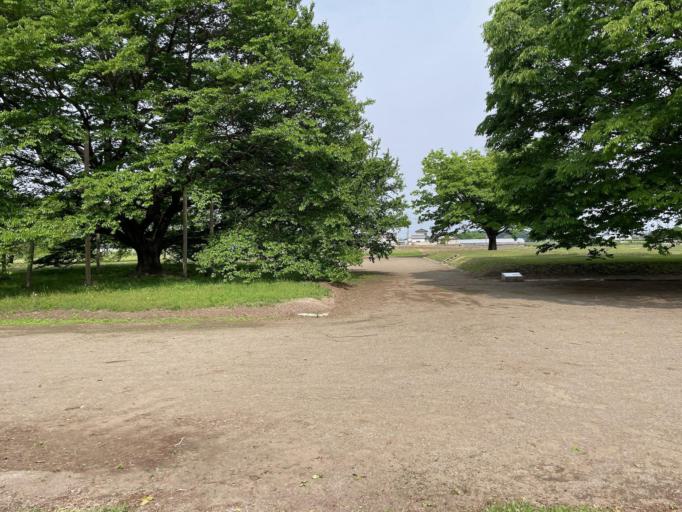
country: JP
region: Tochigi
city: Mibu
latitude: 36.3859
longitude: 139.8121
